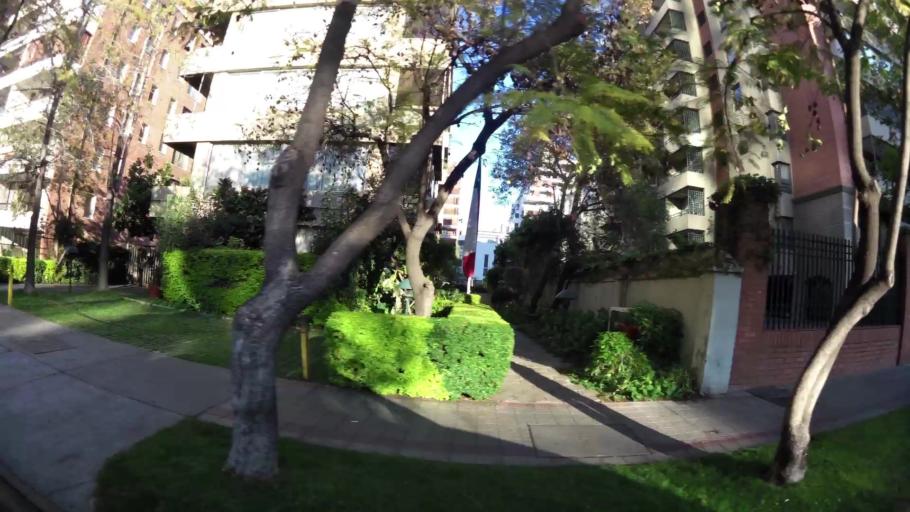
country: CL
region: Santiago Metropolitan
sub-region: Provincia de Santiago
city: Villa Presidente Frei, Nunoa, Santiago, Chile
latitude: -33.4134
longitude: -70.5989
